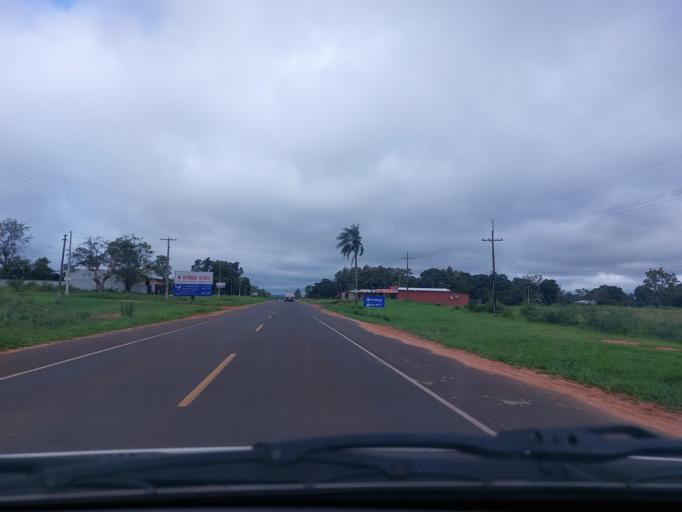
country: PY
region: San Pedro
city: Guayaybi
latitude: -24.6144
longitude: -56.3814
